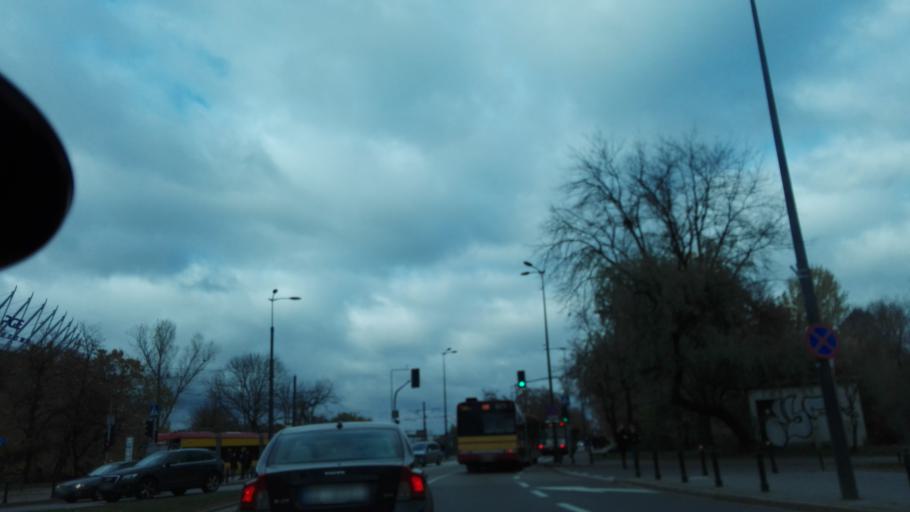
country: PL
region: Masovian Voivodeship
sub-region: Warszawa
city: Praga Polnoc
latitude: 52.2386
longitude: 21.0517
